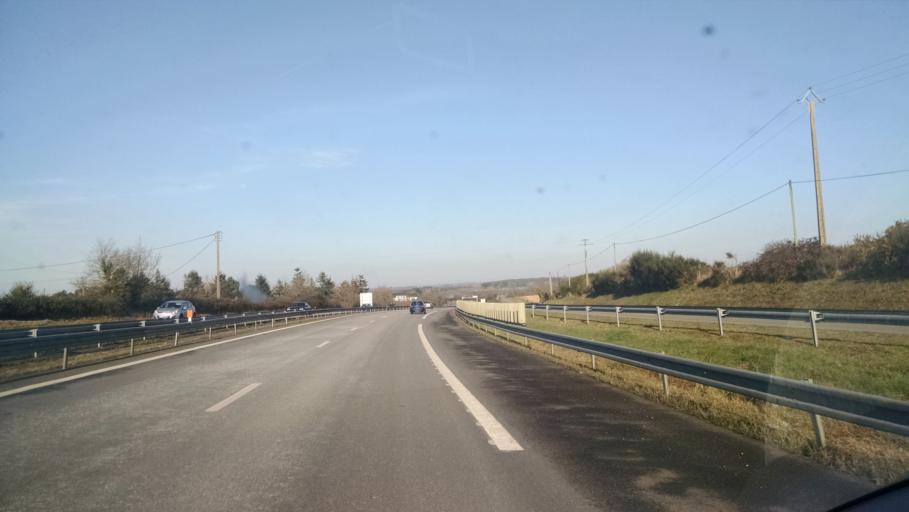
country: FR
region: Brittany
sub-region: Departement du Morbihan
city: Theix
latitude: 47.6218
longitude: -2.6295
